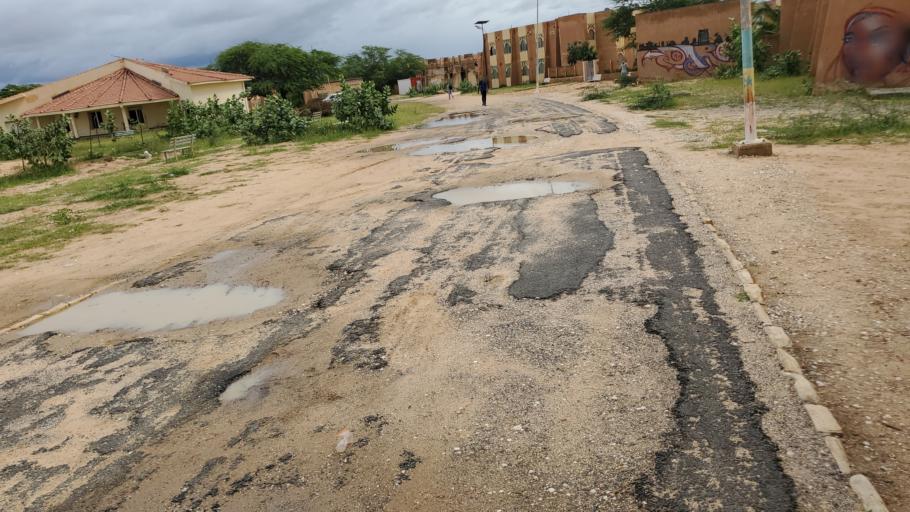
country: SN
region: Saint-Louis
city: Saint-Louis
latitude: 16.0632
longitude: -16.4272
